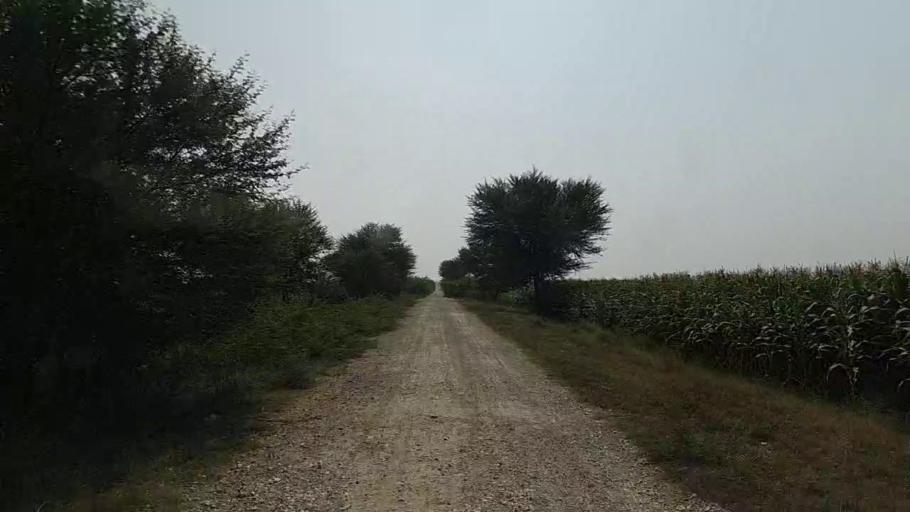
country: PK
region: Sindh
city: Naukot
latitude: 24.8132
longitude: 69.3993
